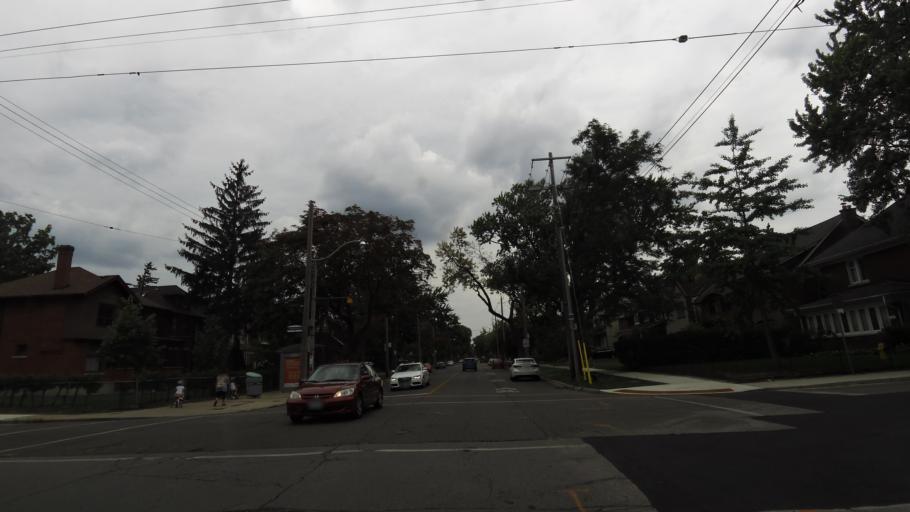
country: CA
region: Ontario
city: Toronto
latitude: 43.6572
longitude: -79.4668
